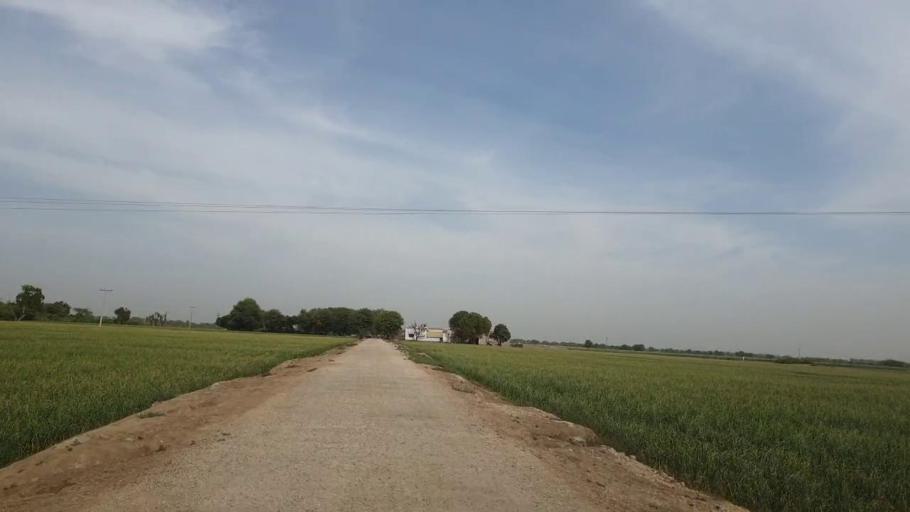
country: PK
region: Sindh
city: Kunri
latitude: 25.1832
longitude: 69.5887
